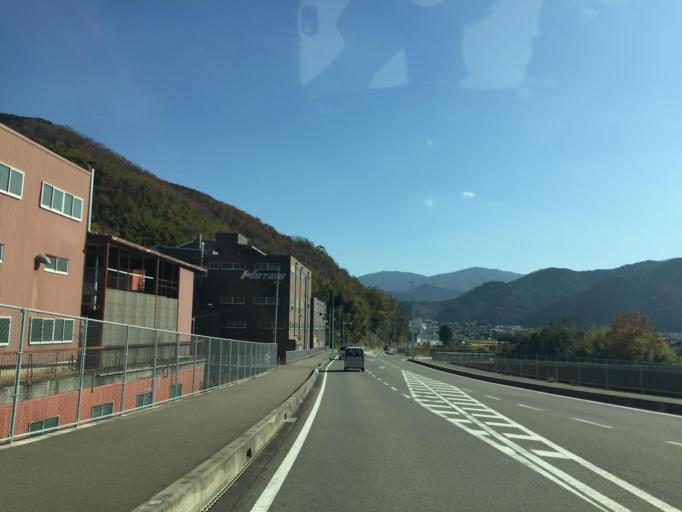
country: JP
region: Wakayama
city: Iwade
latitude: 34.1629
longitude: 135.3069
